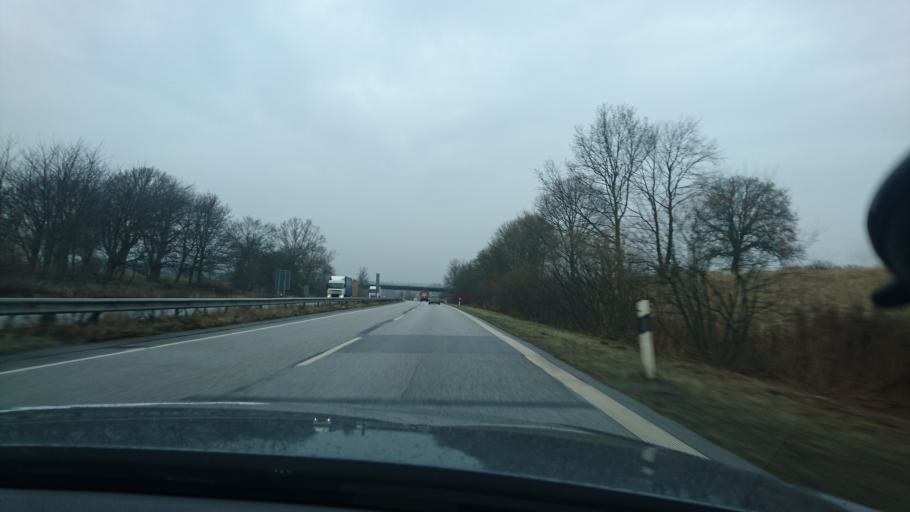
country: DE
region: Schleswig-Holstein
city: Sierksdorf
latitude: 54.0987
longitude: 10.7791
